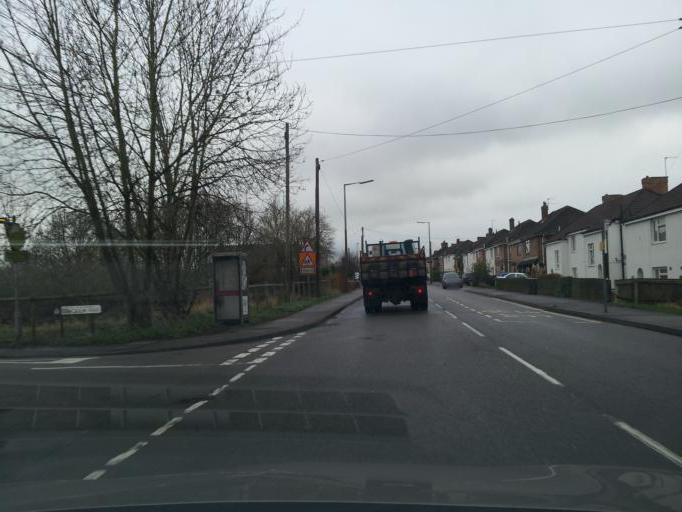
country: GB
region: England
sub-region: Derbyshire
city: Swadlincote
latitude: 52.7779
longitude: -1.5405
